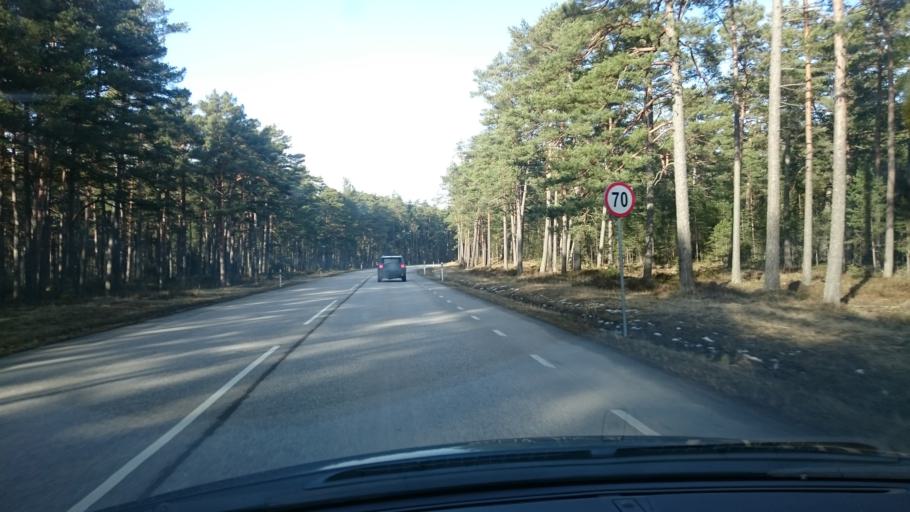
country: EE
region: Harju
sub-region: Keila linn
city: Keila
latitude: 59.4283
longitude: 24.3616
